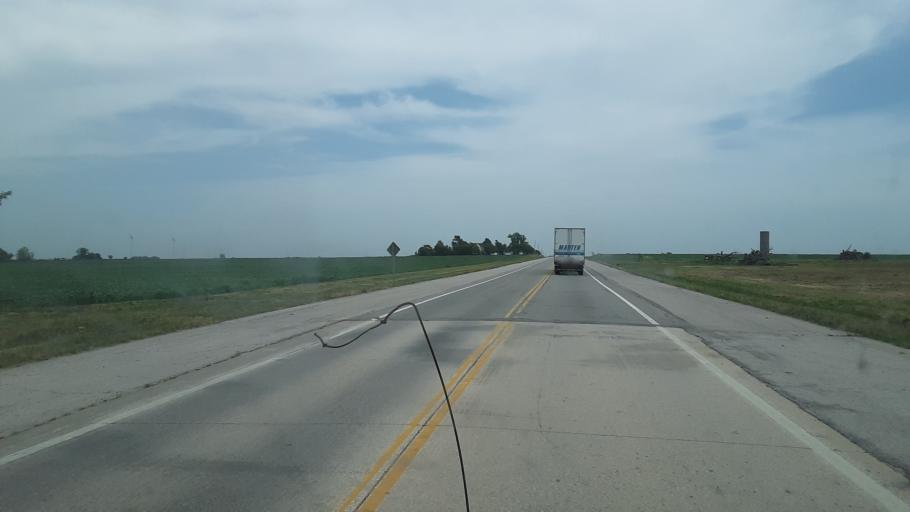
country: US
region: Kansas
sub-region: Allen County
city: Iola
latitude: 37.9220
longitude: -95.2902
